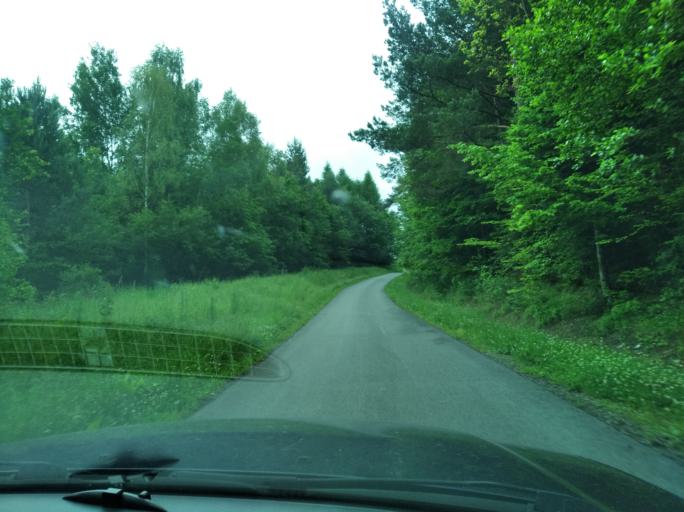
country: PL
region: Subcarpathian Voivodeship
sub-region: Powiat przemyski
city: Dubiecko
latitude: 49.8713
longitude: 22.4049
